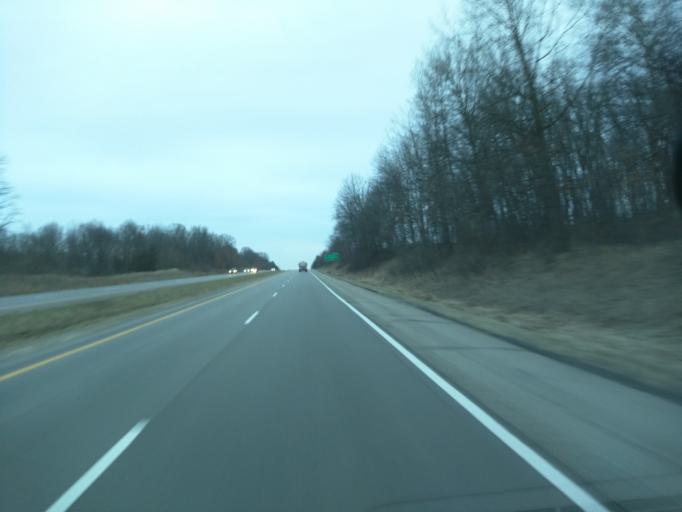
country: US
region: Michigan
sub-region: Ingham County
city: Leslie
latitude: 42.4000
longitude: -84.4292
